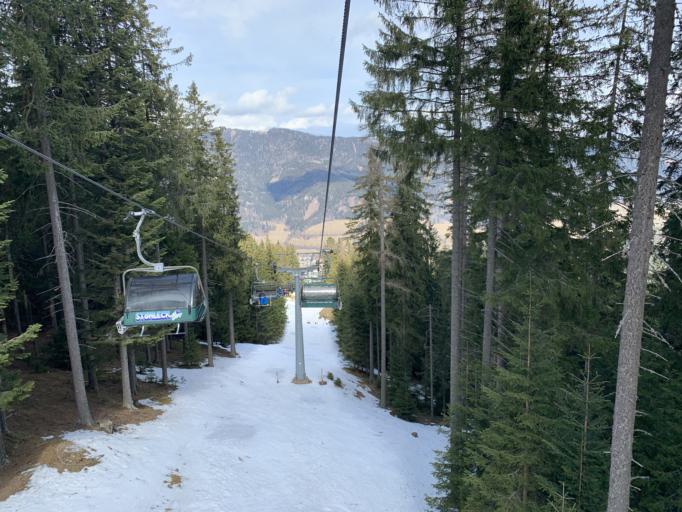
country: AT
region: Styria
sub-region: Politischer Bezirk Bruck-Muerzzuschlag
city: Spital am Semmering
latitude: 47.5954
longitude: 15.7632
